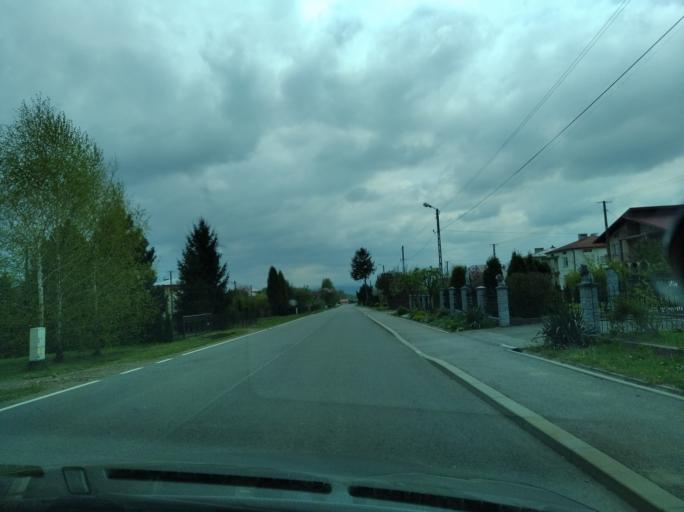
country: PL
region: Subcarpathian Voivodeship
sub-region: Powiat brzozowski
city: Jasionow
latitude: 49.6487
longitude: 21.9770
